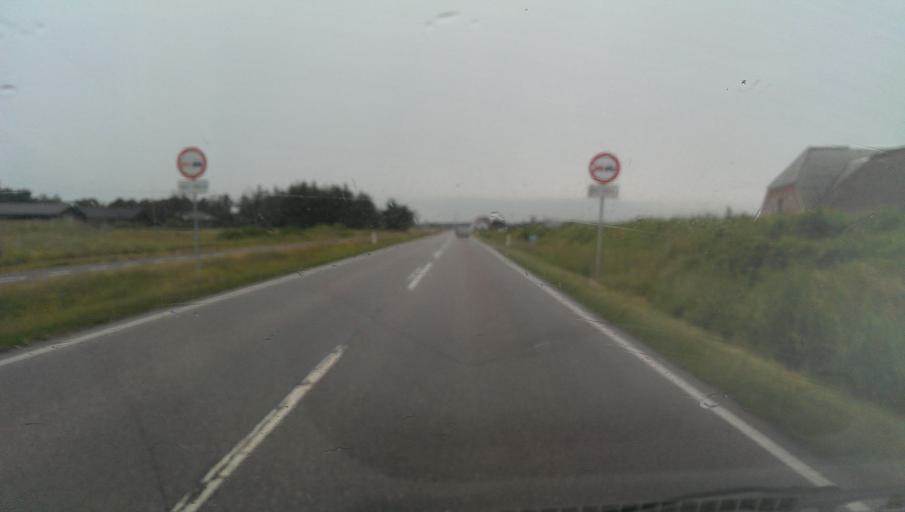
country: DK
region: Central Jutland
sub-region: Ringkobing-Skjern Kommune
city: Hvide Sande
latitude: 56.0773
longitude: 8.1203
